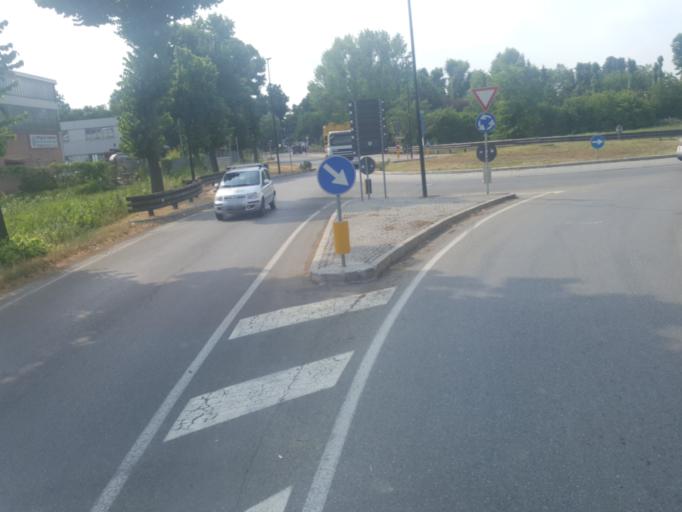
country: IT
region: Emilia-Romagna
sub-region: Provincia di Modena
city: Castelfranco Emilia
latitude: 44.5877
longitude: 11.0736
